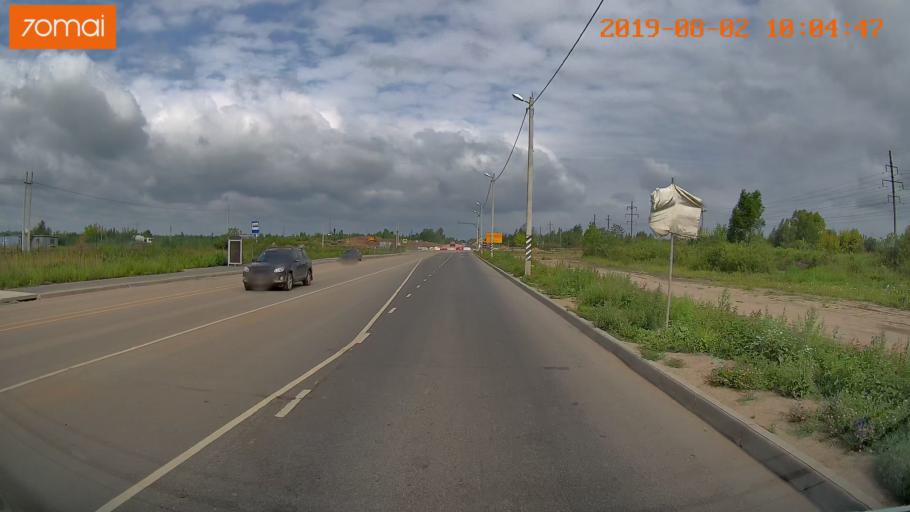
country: RU
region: Ivanovo
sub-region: Gorod Ivanovo
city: Ivanovo
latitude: 56.9754
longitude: 40.9226
